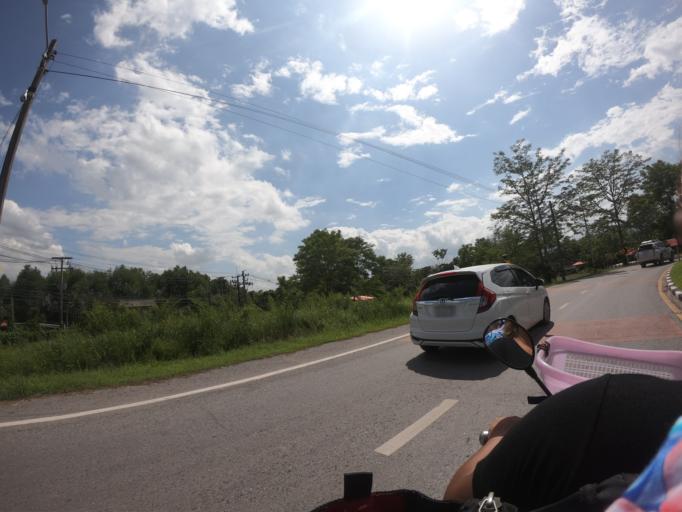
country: TH
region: Nakhon Nayok
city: Nakhon Nayok
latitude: 14.3110
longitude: 101.3155
